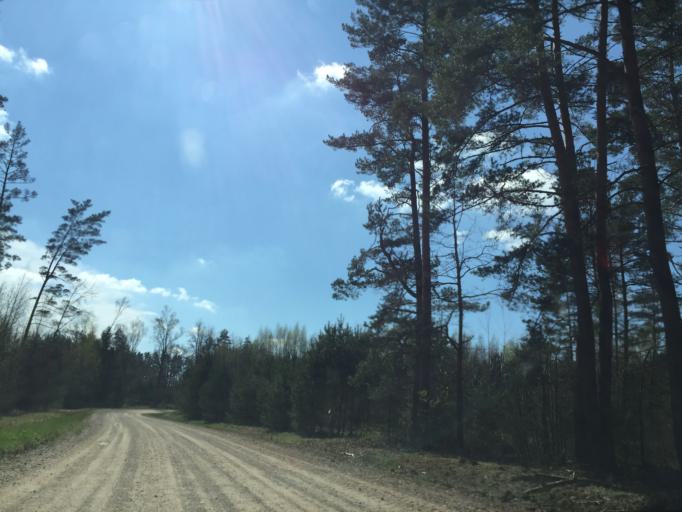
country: LV
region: Smiltene
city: Smiltene
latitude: 57.5758
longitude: 25.9306
